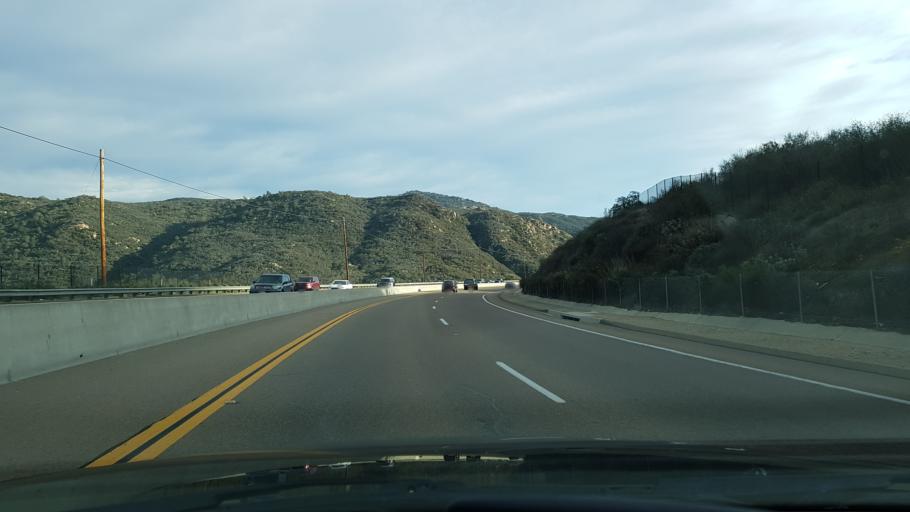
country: US
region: California
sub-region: San Diego County
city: Valley Center
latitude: 33.1830
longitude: -117.0251
